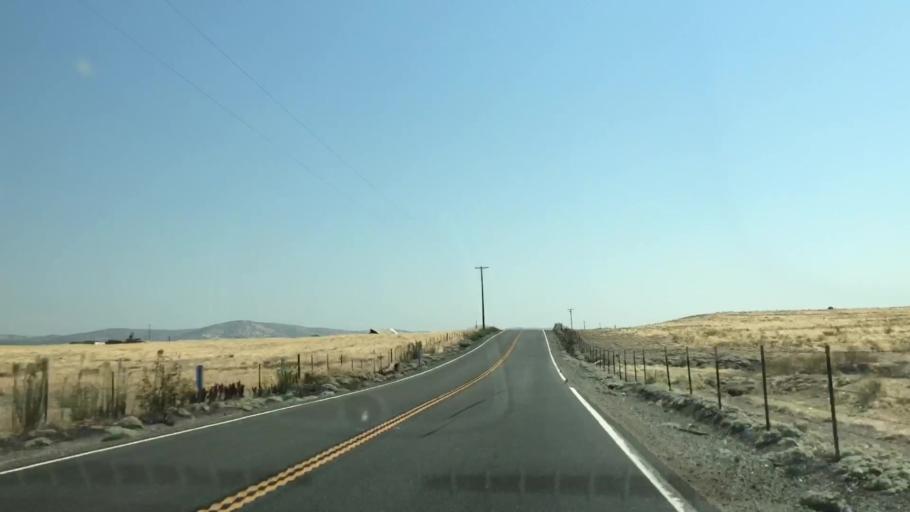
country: US
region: California
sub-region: Stanislaus County
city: East Oakdale
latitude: 37.9412
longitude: -120.8185
